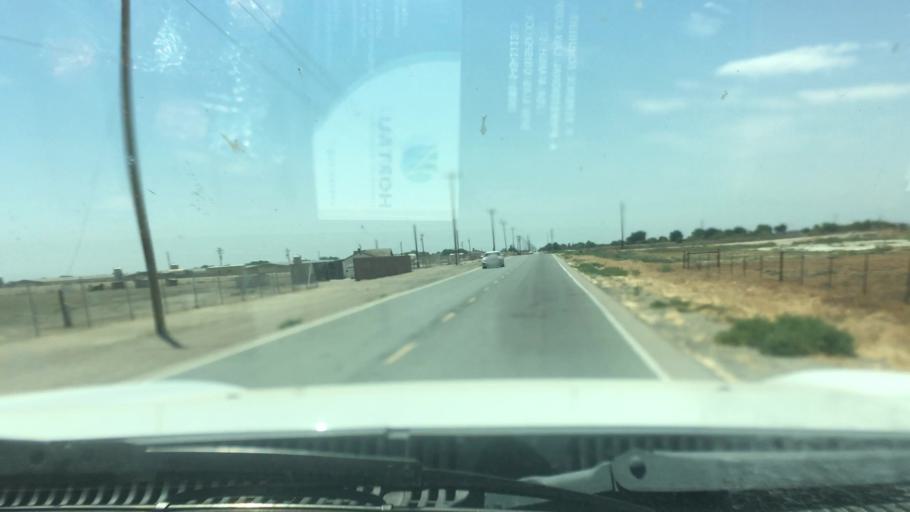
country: US
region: California
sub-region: Kings County
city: Corcoran
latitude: 36.0508
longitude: -119.4854
